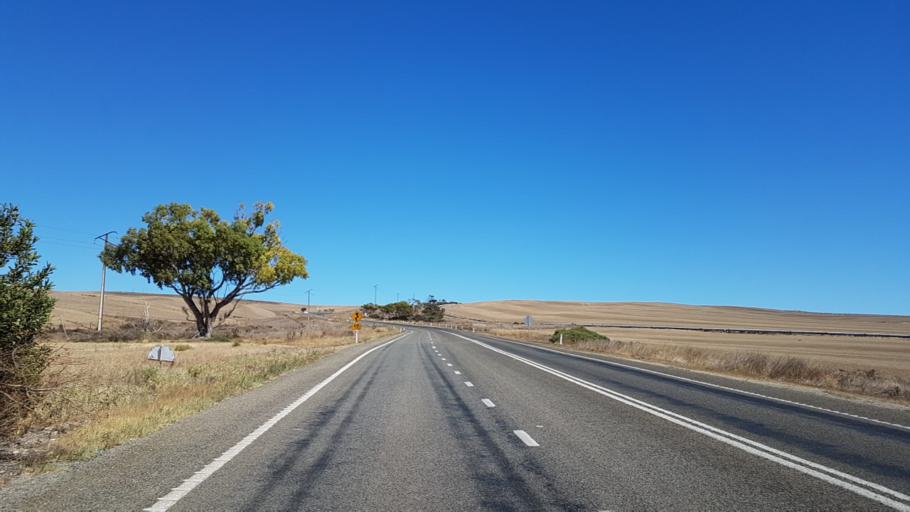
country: AU
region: South Australia
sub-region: Wakefield
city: Balaklava
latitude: -34.0685
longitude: 138.0645
